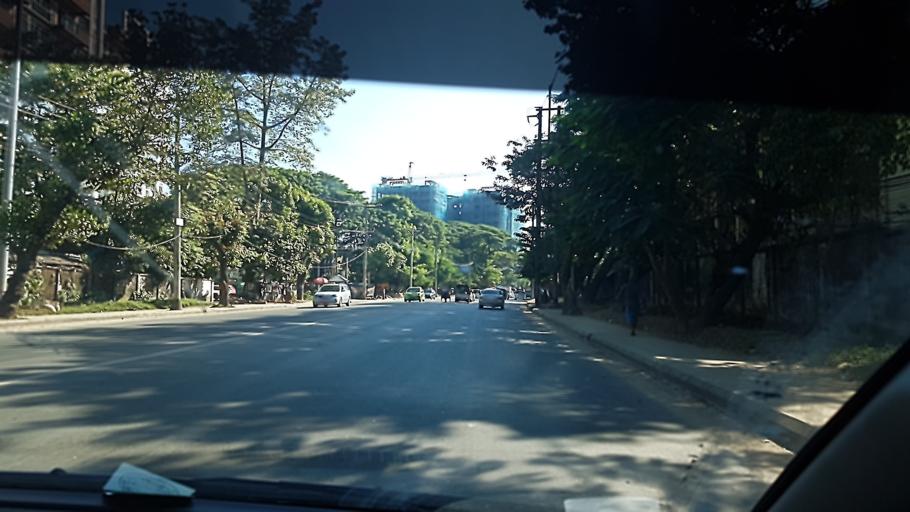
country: MM
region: Yangon
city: Yangon
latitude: 16.8577
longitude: 96.1267
